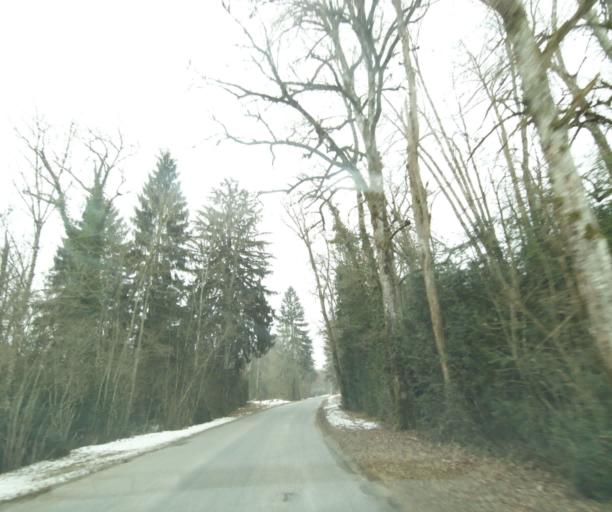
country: FR
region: Rhone-Alpes
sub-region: Departement de la Haute-Savoie
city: Cornier
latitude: 46.1179
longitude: 6.2914
